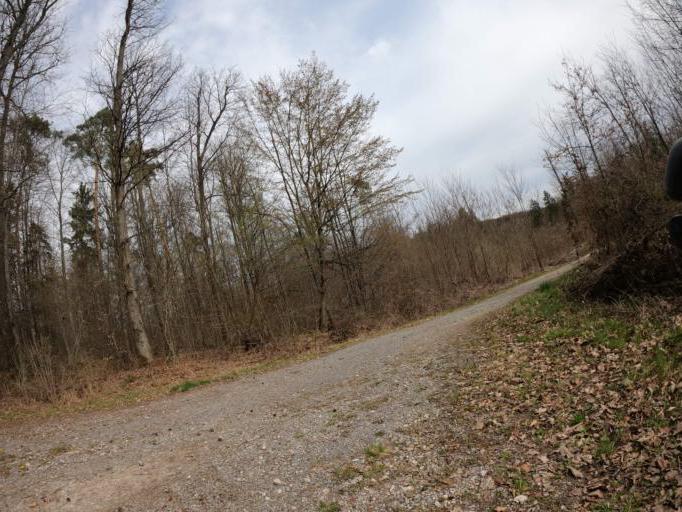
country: DE
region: Baden-Wuerttemberg
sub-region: Regierungsbezirk Stuttgart
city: Filderstadt
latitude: 48.6407
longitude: 9.1830
